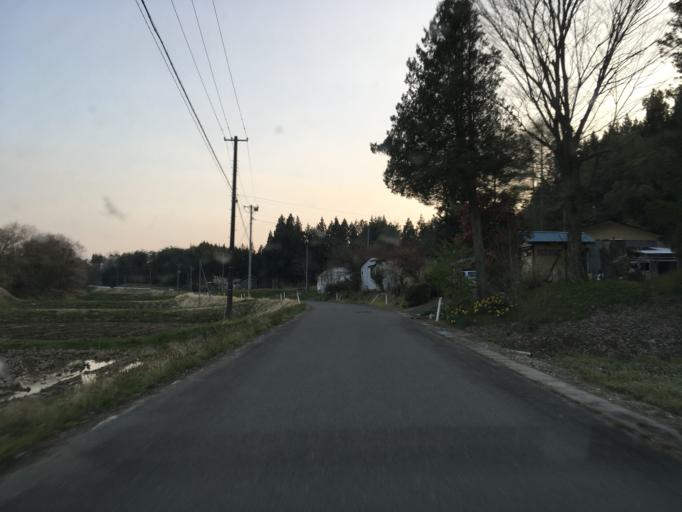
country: JP
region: Iwate
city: Ichinoseki
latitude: 38.8340
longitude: 141.1047
